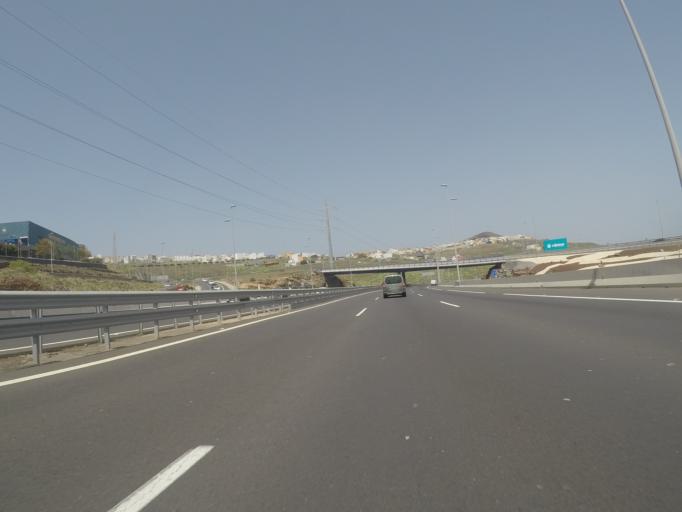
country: ES
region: Canary Islands
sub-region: Provincia de Santa Cruz de Tenerife
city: La Laguna
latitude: 28.4274
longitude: -16.3034
